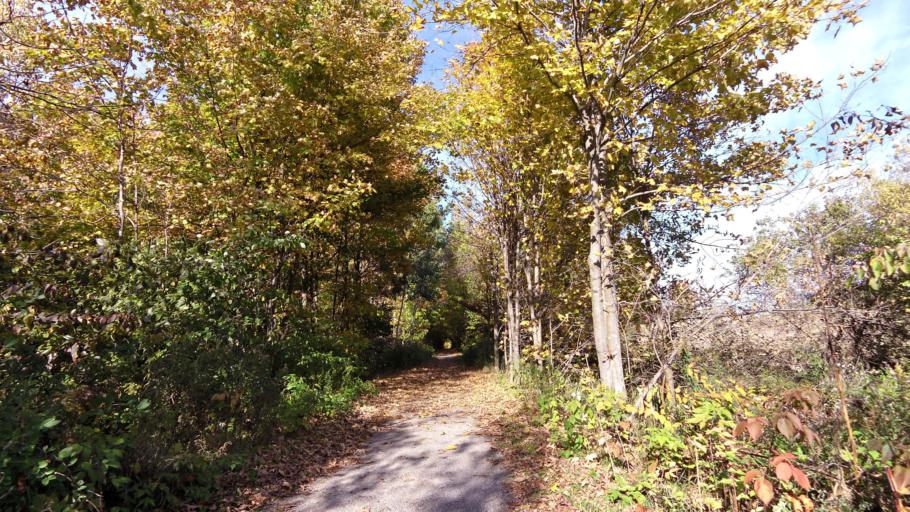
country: CA
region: Ontario
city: Orangeville
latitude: 43.8053
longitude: -80.0336
